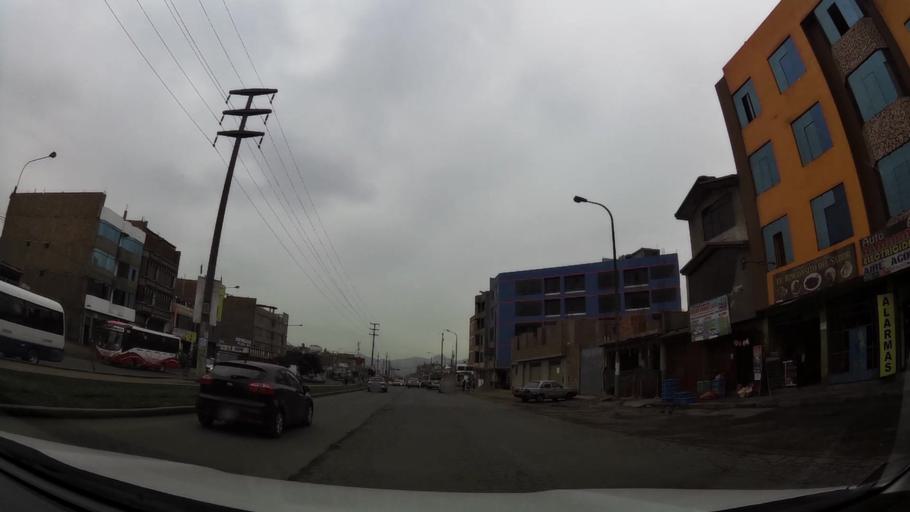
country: PE
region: Lima
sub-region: Lima
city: Vitarte
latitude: -12.0373
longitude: -76.9530
